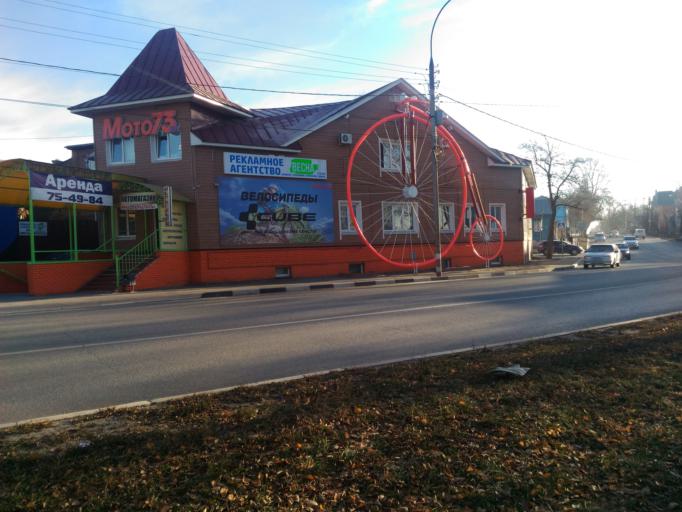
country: RU
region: Ulyanovsk
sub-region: Ulyanovskiy Rayon
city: Ulyanovsk
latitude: 54.3129
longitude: 48.3789
